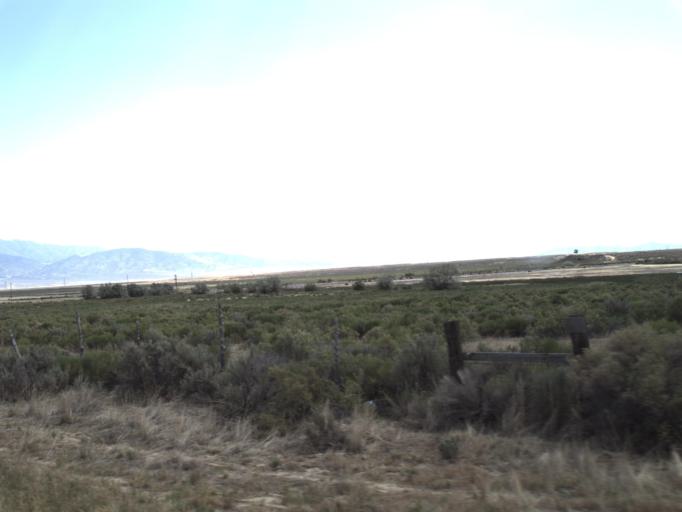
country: US
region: Utah
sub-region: Tooele County
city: Tooele
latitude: 40.1776
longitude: -112.4256
